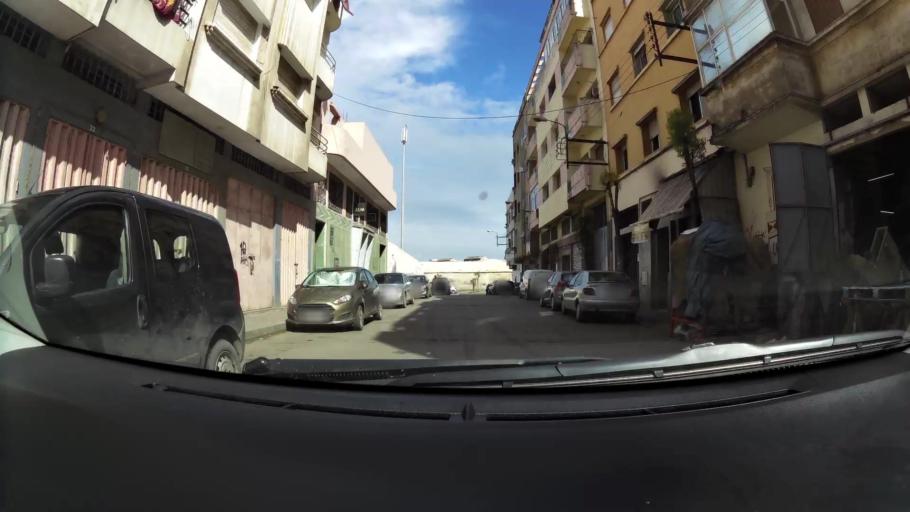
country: MA
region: Grand Casablanca
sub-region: Casablanca
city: Casablanca
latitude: 33.5869
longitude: -7.5795
